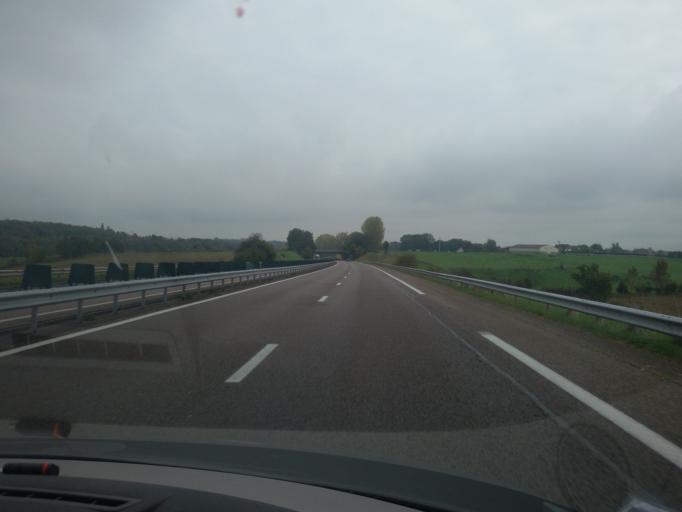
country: FR
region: Haute-Normandie
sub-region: Departement de l'Eure
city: Manneville-sur-Risle
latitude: 49.3860
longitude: 0.5656
